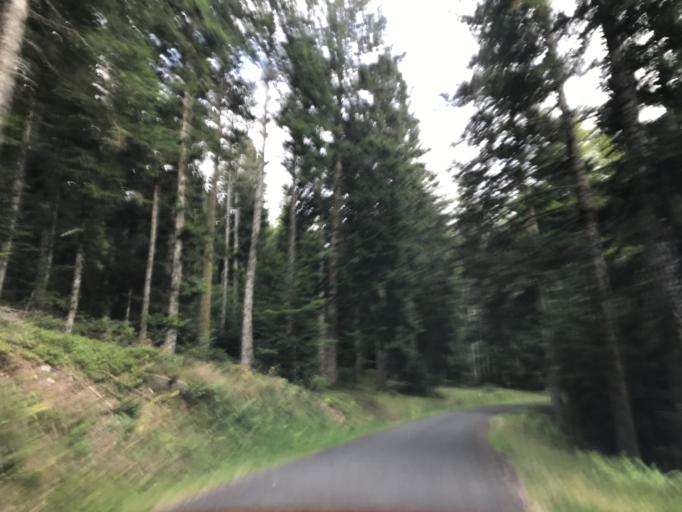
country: FR
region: Rhone-Alpes
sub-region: Departement de la Loire
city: Noiretable
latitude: 45.7647
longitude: 3.7274
